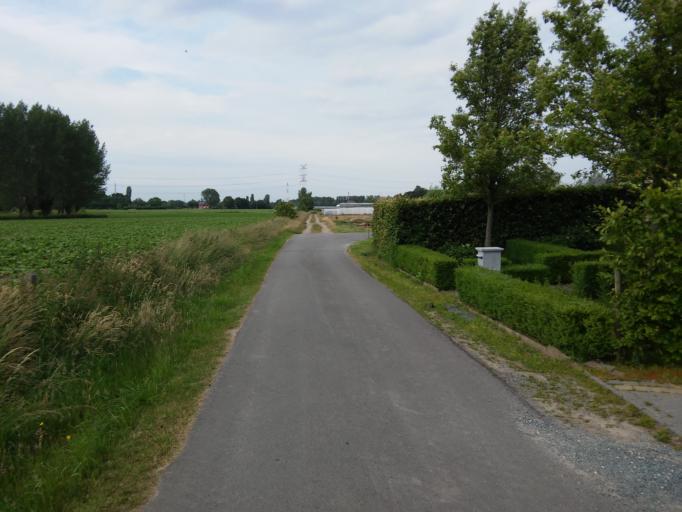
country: BE
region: Flanders
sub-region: Provincie Antwerpen
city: Rumst
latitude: 51.1041
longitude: 4.4231
